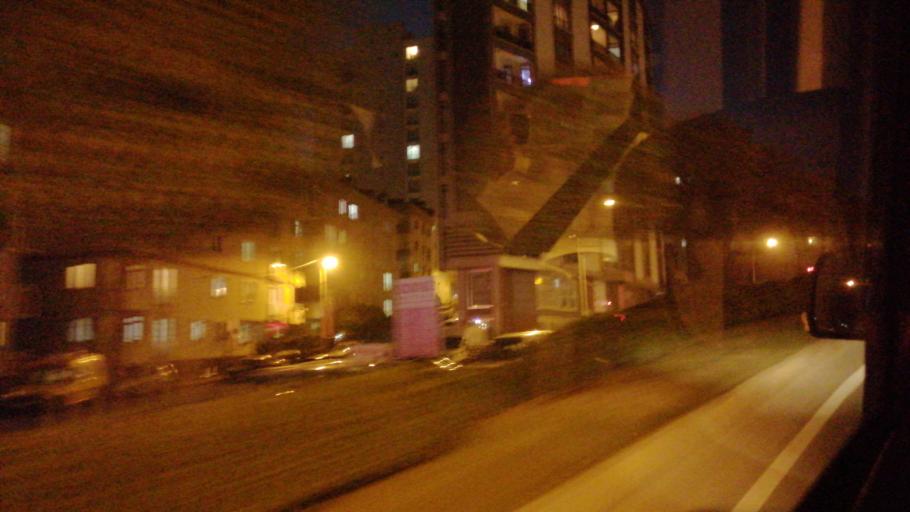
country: TR
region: Istanbul
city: Umraniye
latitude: 41.0075
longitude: 29.1284
